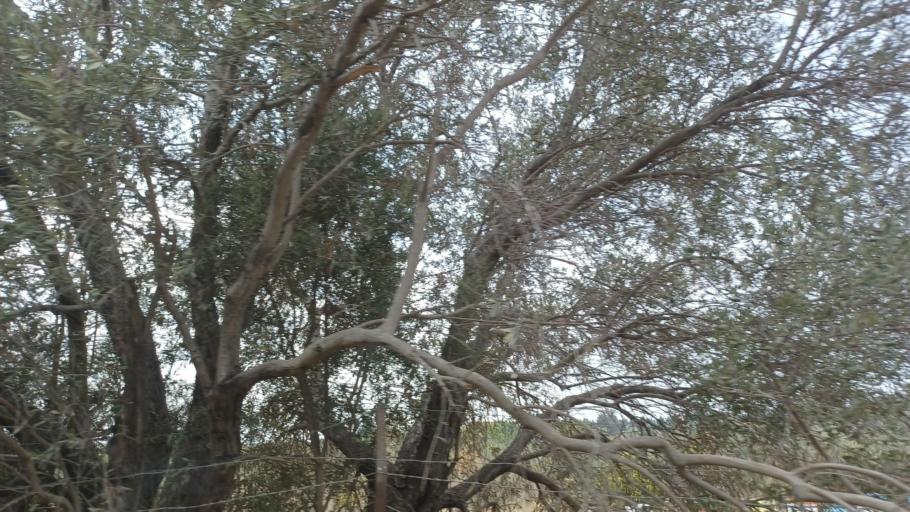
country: CY
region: Larnaka
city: Kolossi
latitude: 34.6642
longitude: 32.9481
